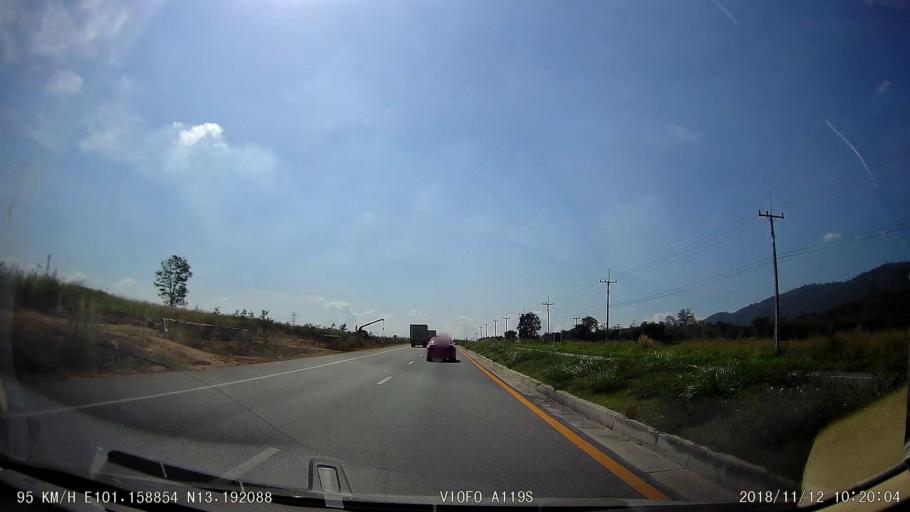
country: TH
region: Chon Buri
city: Ban Bueng
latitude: 13.1915
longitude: 101.1590
